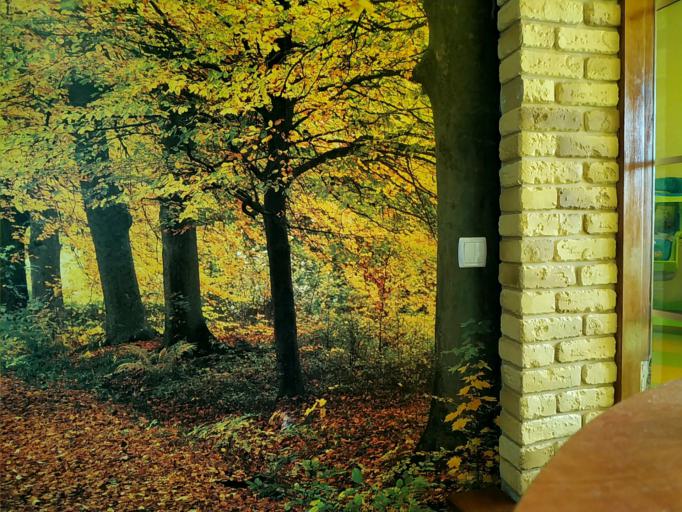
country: RU
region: Novgorod
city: Staraya Russa
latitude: 57.8378
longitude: 31.4641
